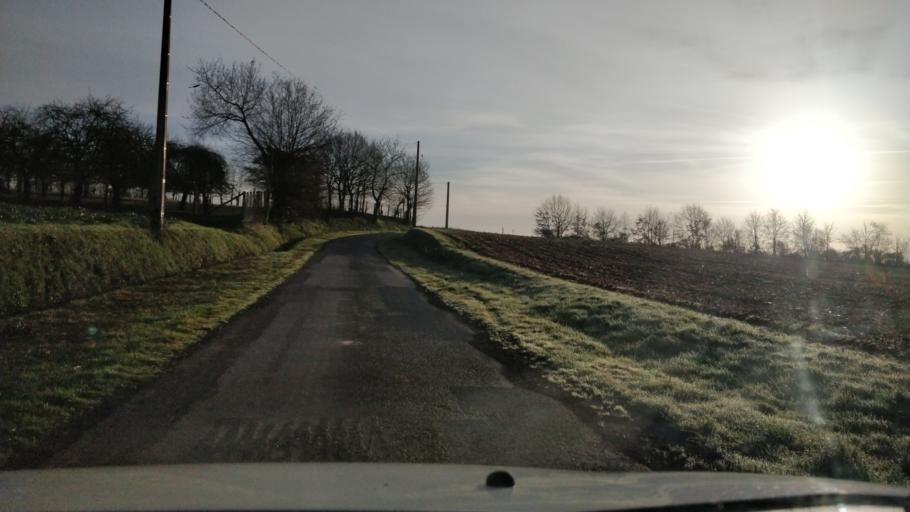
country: FR
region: Brittany
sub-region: Departement d'Ille-et-Vilaine
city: Bais
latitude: 48.0147
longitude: -1.3155
